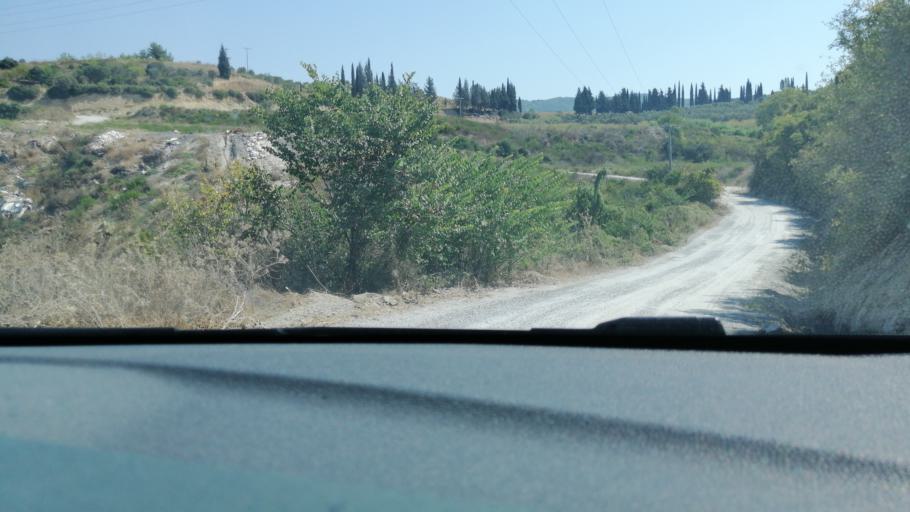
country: TR
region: Aydin
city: Davutlar
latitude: 37.7834
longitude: 27.3145
